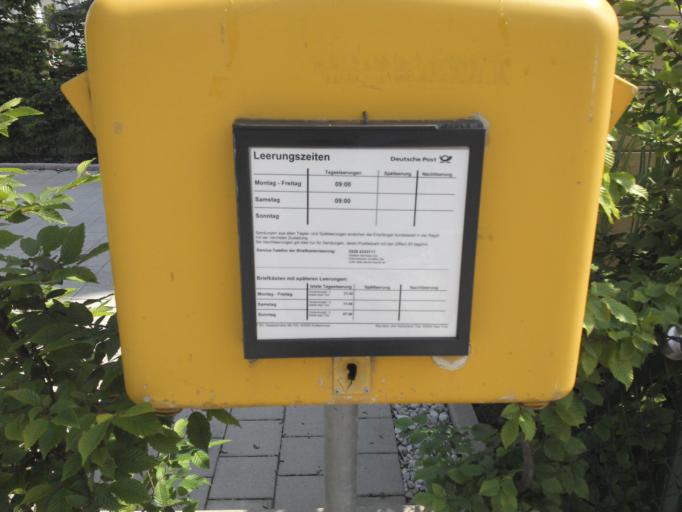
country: DE
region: Bavaria
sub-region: Upper Bavaria
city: Bad Toelz
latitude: 47.7644
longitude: 11.5398
